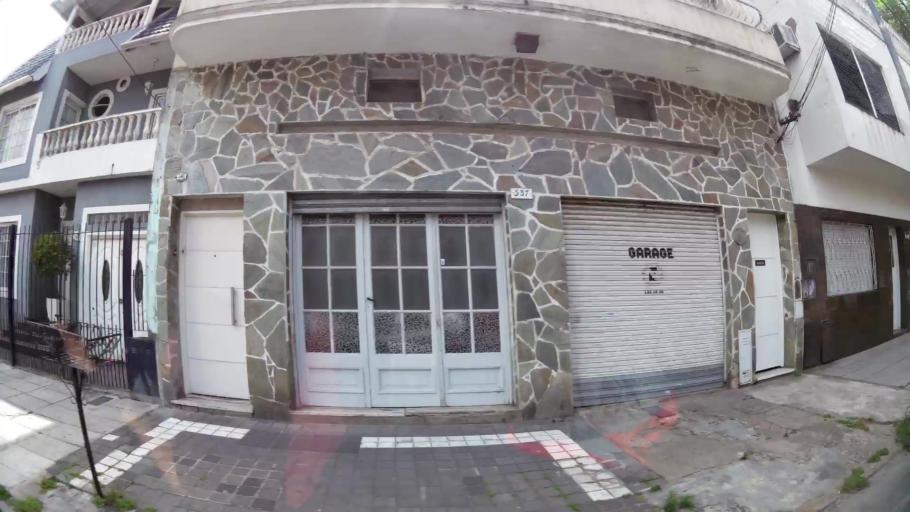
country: AR
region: Buenos Aires
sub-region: Partido de Lanus
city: Lanus
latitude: -34.6679
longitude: -58.4112
